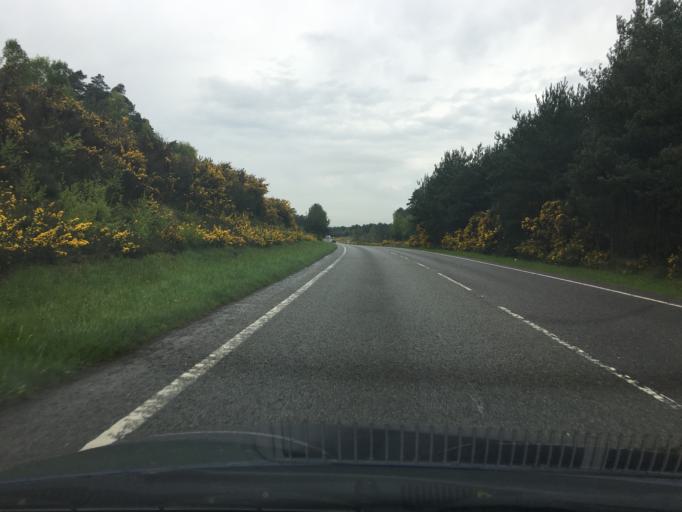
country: GB
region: England
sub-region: Bracknell Forest
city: Crowthorne
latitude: 51.3740
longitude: -0.7668
